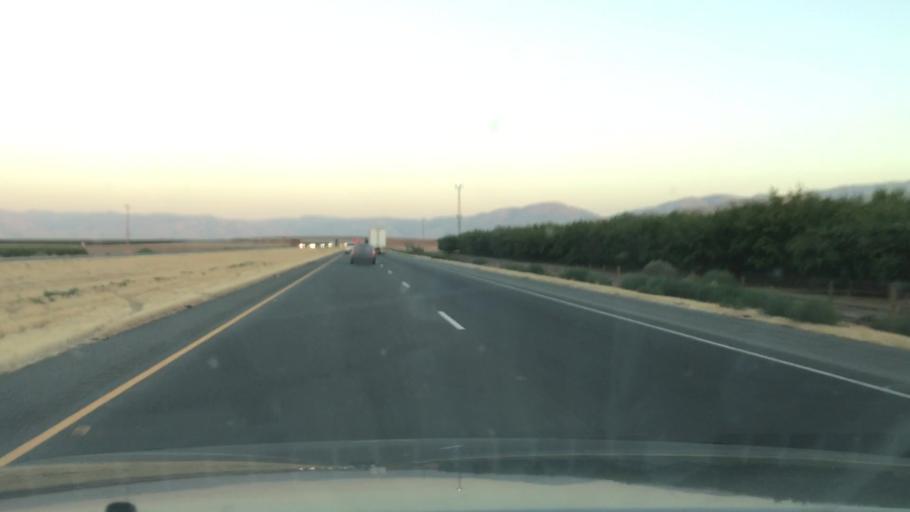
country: US
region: California
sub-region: Kern County
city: Greenfield
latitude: 35.0812
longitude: -119.0217
